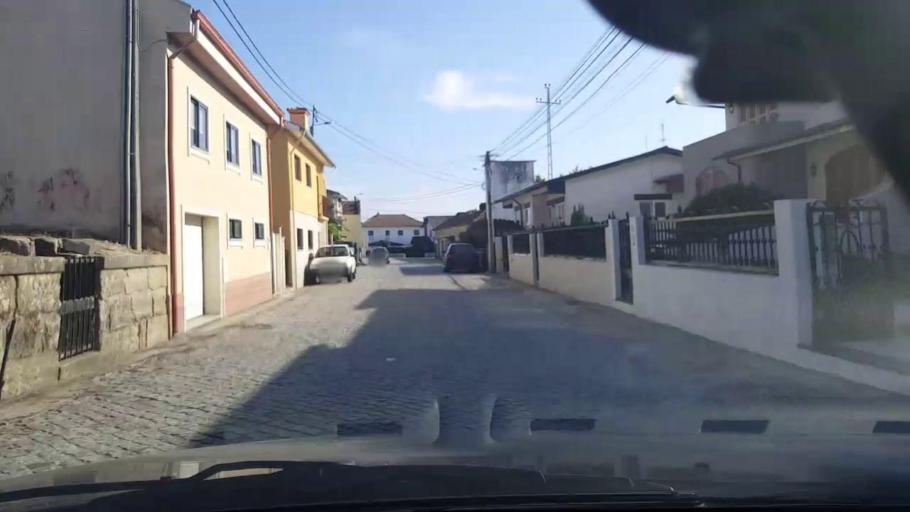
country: PT
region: Porto
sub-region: Maia
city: Gemunde
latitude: 41.2706
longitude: -8.6646
